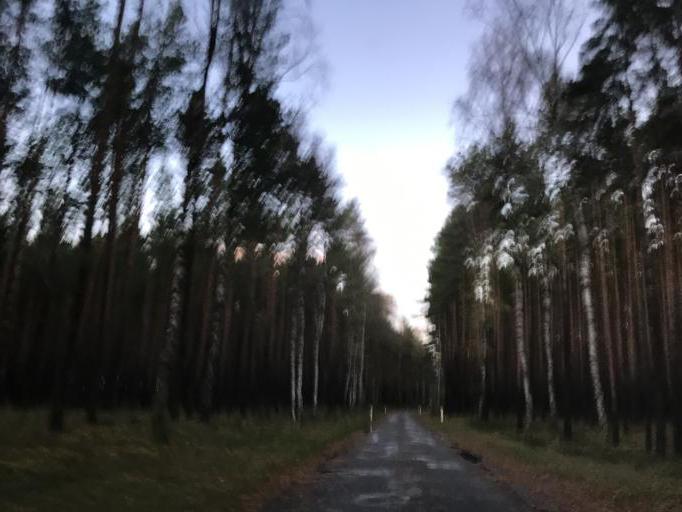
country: DE
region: Mecklenburg-Vorpommern
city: Wesenberg
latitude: 53.2887
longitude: 12.8878
